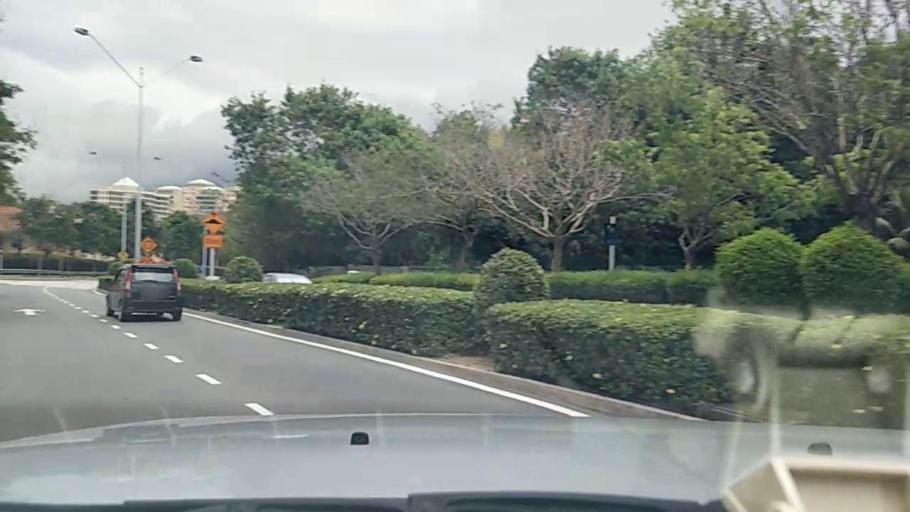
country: MY
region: Putrajaya
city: Putrajaya
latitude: 2.9299
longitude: 101.7011
